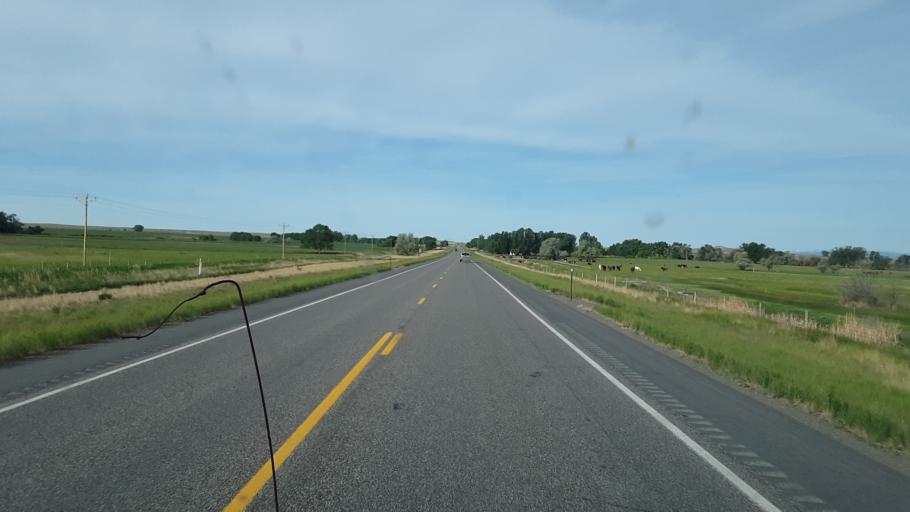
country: US
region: Wyoming
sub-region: Fremont County
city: Riverton
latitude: 43.1817
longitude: -108.2495
